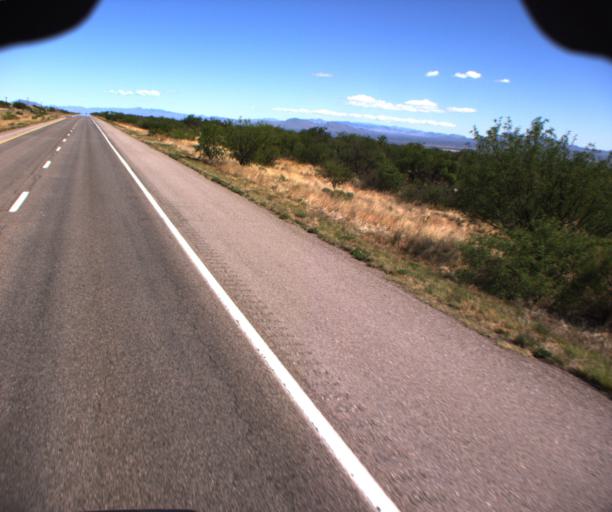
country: US
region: Arizona
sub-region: Cochise County
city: Whetstone
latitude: 31.8656
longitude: -110.3410
